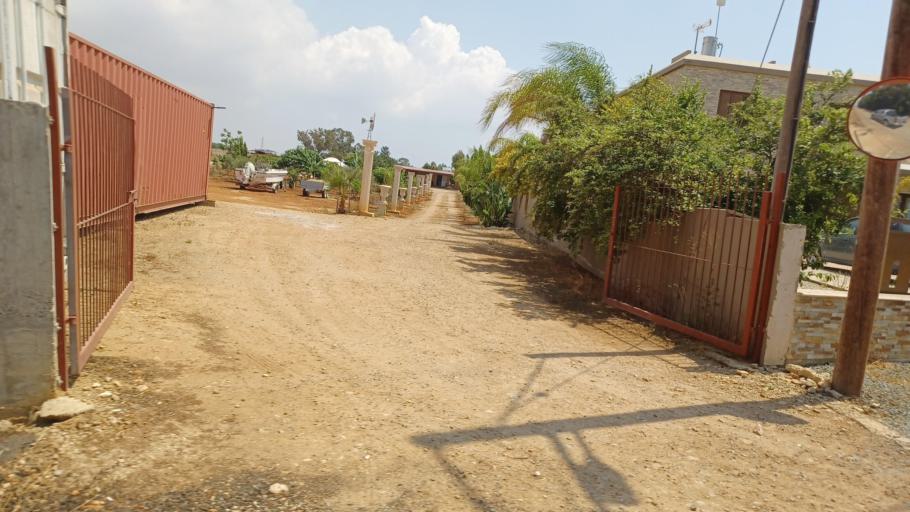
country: CY
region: Ammochostos
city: Liopetri
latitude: 34.9897
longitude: 33.8578
